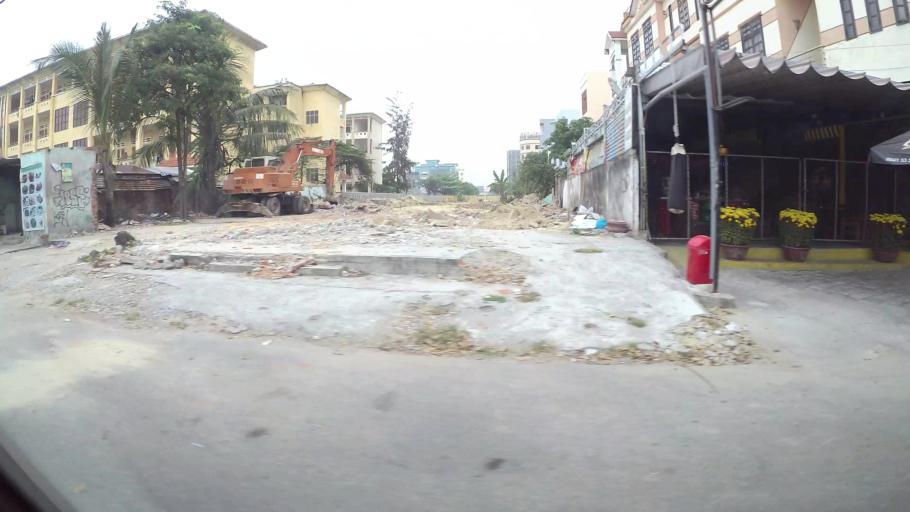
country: VN
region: Da Nang
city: Son Tra
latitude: 16.0462
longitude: 108.2444
